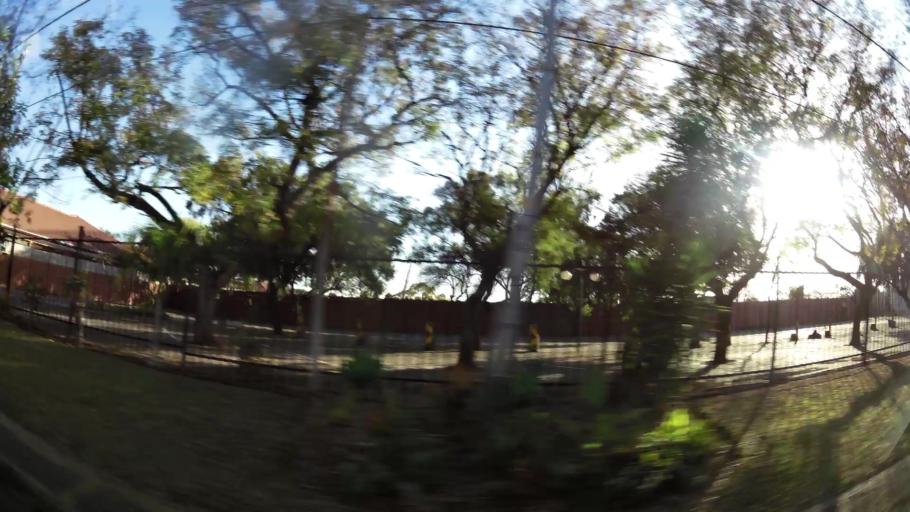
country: ZA
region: Gauteng
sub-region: City of Tshwane Metropolitan Municipality
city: Pretoria
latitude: -25.7127
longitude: 28.2093
